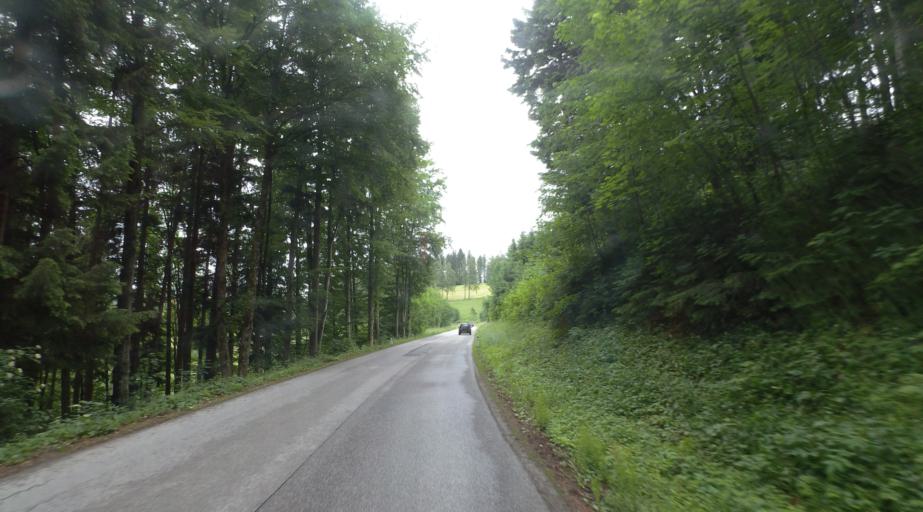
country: AT
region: Upper Austria
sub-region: Politischer Bezirk Kirchdorf an der Krems
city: Micheldorf in Oberoesterreich
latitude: 47.9273
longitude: 14.1693
